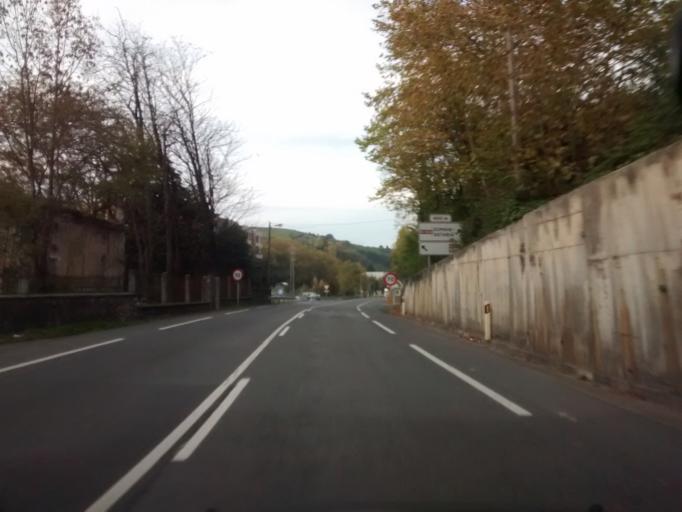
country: ES
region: Basque Country
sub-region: Provincia de Guipuzcoa
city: Zumaia
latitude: 43.2768
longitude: -2.2676
